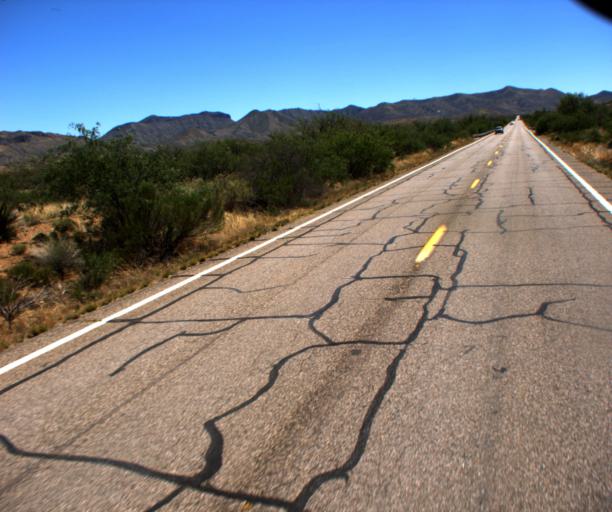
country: US
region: Arizona
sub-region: Pima County
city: Vail
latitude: 31.9539
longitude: -110.6682
